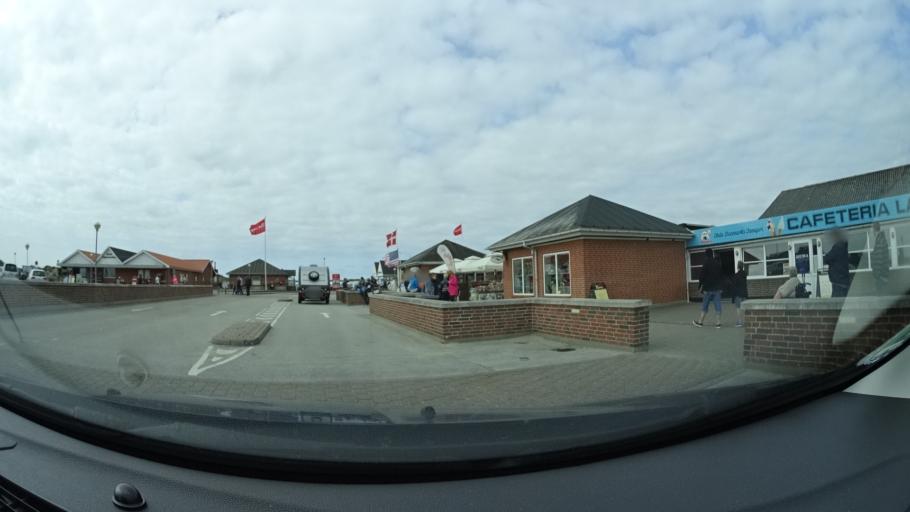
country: DE
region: Schleswig-Holstein
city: List
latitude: 55.1458
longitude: 8.4945
